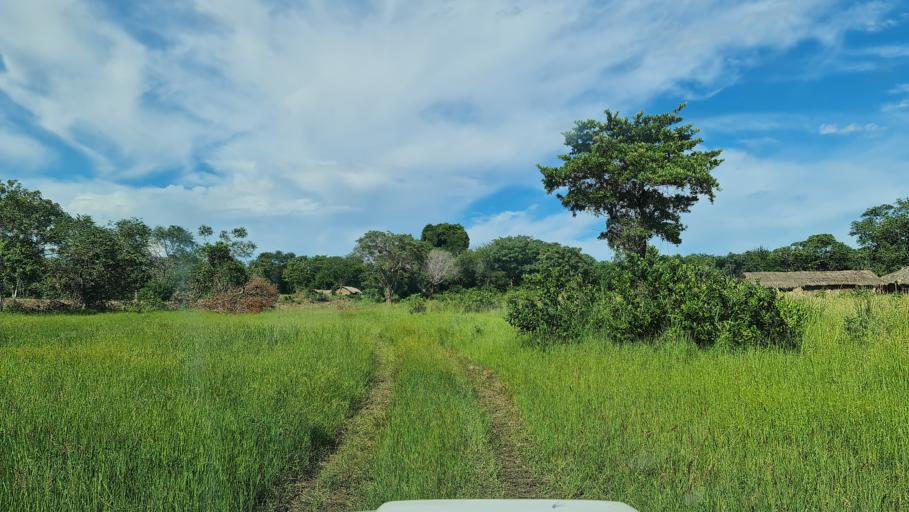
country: MZ
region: Nampula
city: Ilha de Mocambique
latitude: -15.5084
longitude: 40.1421
